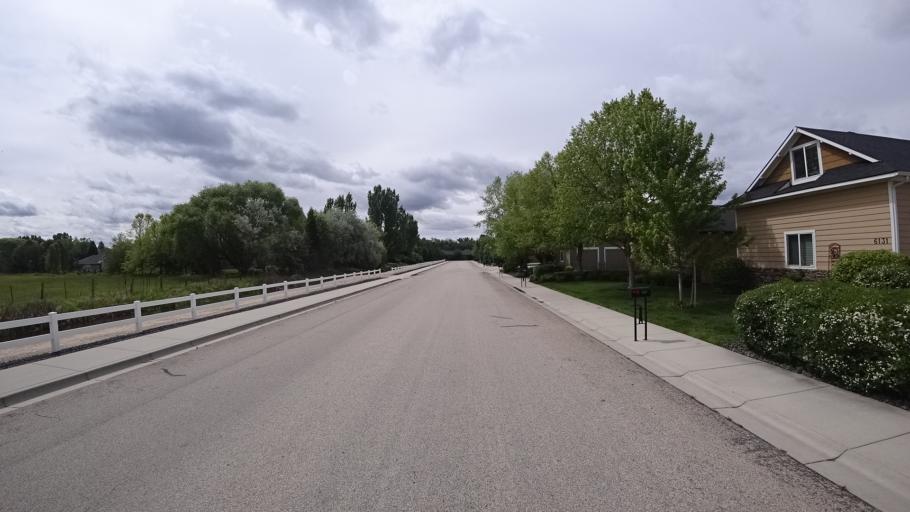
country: US
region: Idaho
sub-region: Ada County
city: Eagle
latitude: 43.6759
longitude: -116.3044
